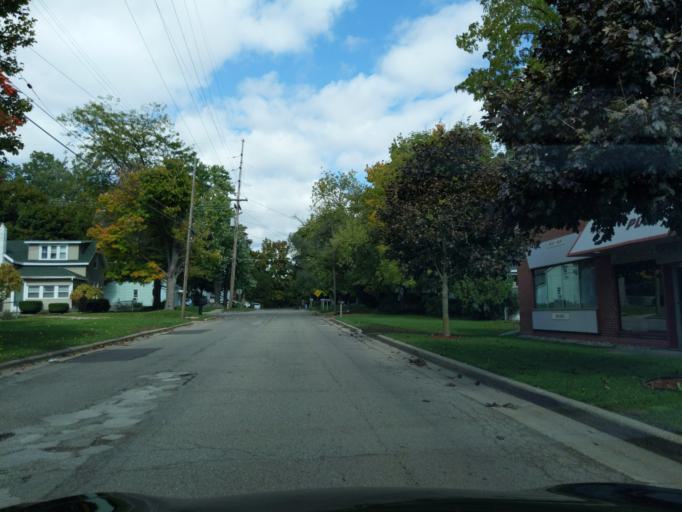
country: US
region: Michigan
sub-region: Eaton County
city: Charlotte
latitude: 42.5697
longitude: -84.8347
